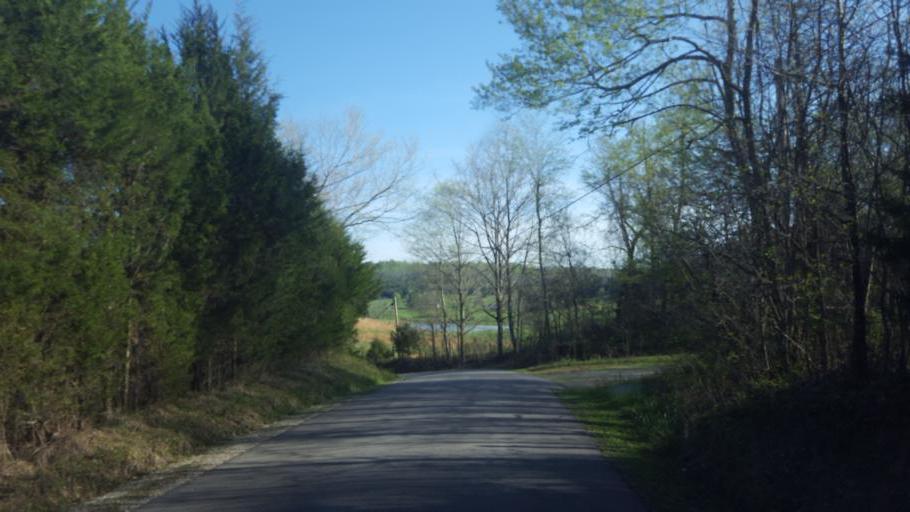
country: US
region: Kentucky
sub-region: Barren County
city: Cave City
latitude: 37.1885
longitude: -86.0128
